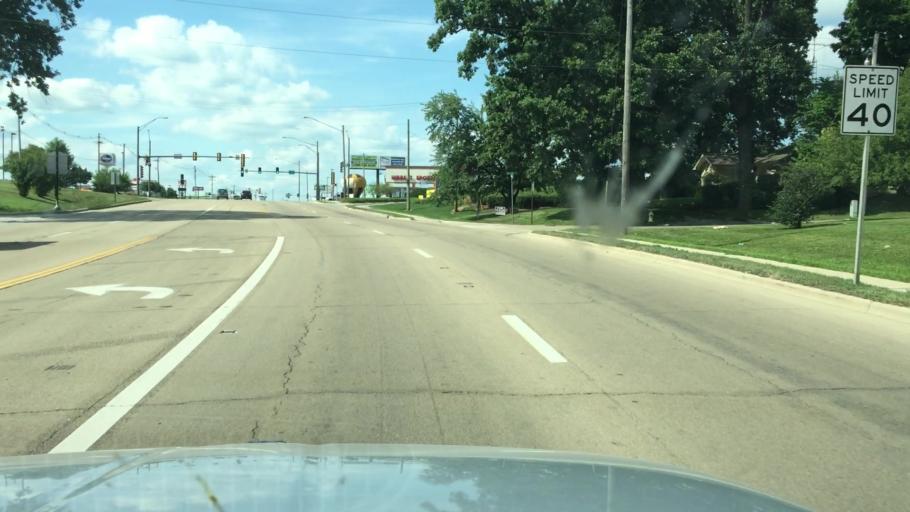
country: US
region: Illinois
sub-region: LaSalle County
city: Ottawa
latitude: 41.3685
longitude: -88.8355
